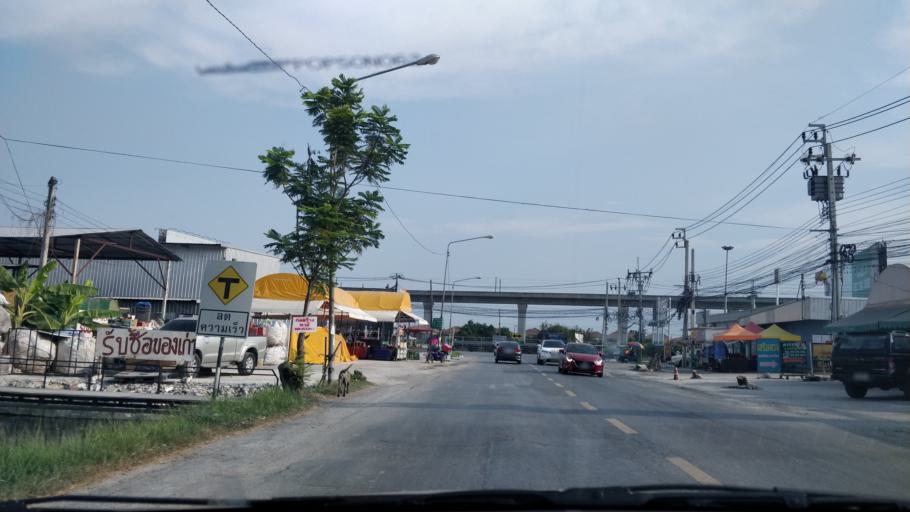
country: TH
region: Bangkok
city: Saphan Sung
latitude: 13.7325
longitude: 100.7163
